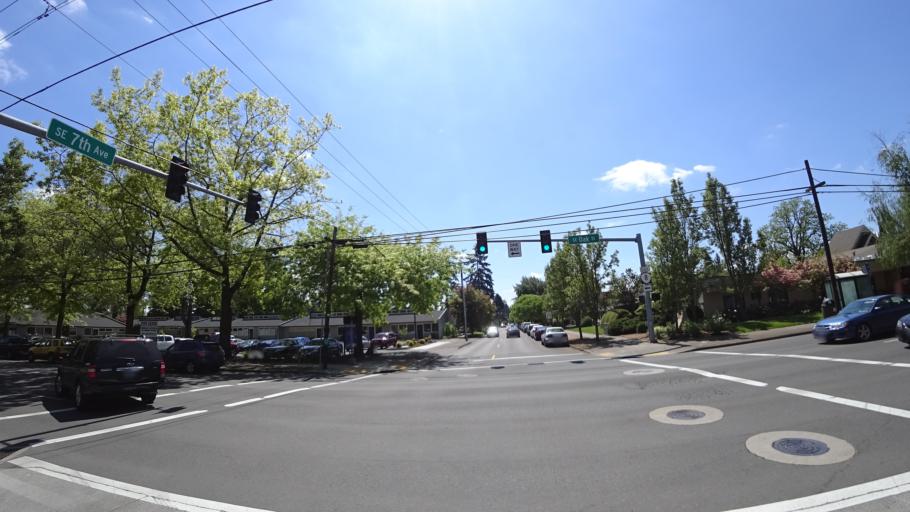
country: US
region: Oregon
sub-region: Washington County
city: Hillsboro
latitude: 45.5189
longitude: -122.9791
